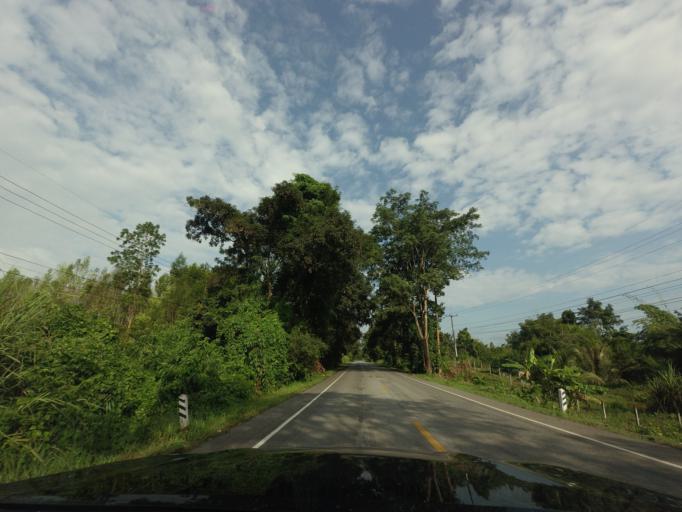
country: TH
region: Nong Khai
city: Pho Tak
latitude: 17.8037
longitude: 102.3435
